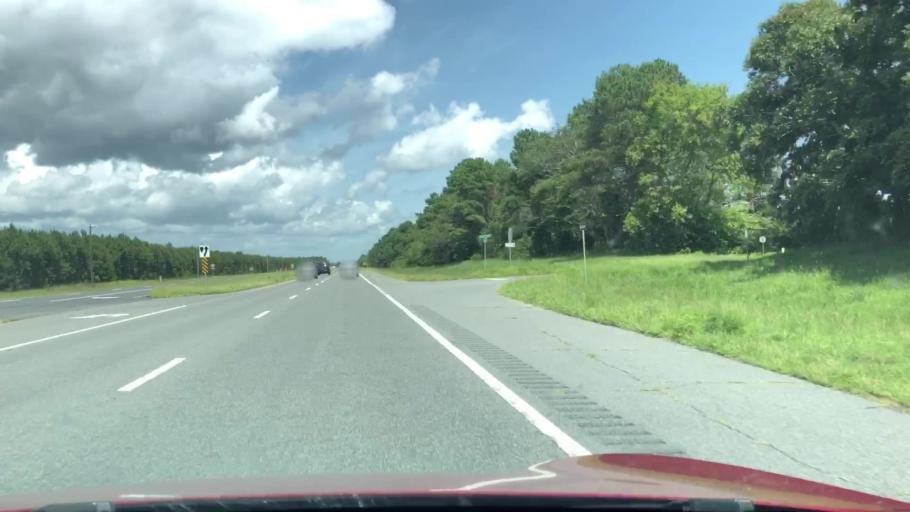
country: US
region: Virginia
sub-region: Northampton County
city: Cape Charles
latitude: 37.1548
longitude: -75.9712
